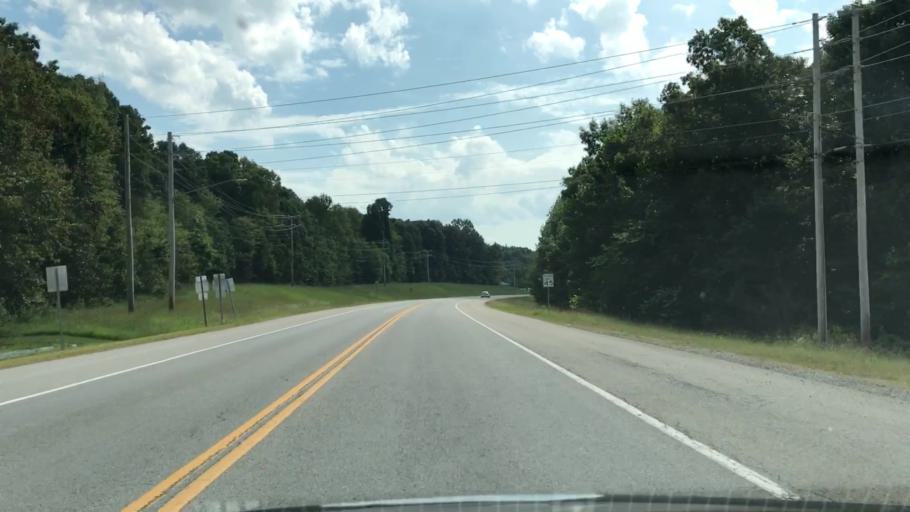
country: US
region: Tennessee
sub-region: Sumner County
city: Westmoreland
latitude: 36.5526
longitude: -86.2330
